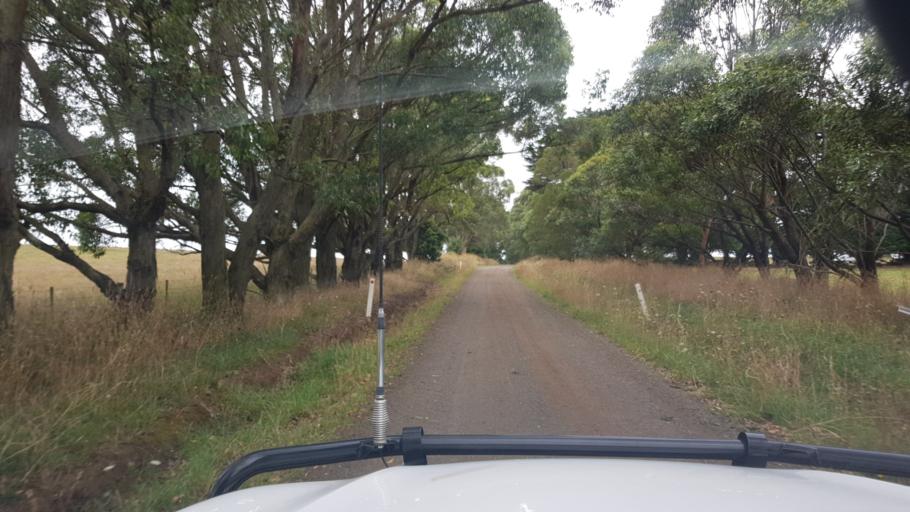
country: AU
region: Victoria
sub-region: Baw Baw
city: Warragul
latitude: -38.2141
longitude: 145.8582
